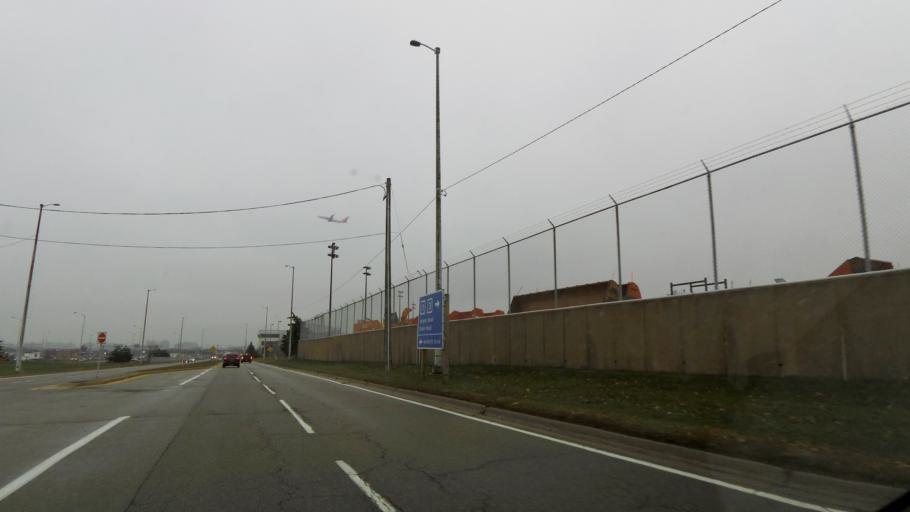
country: CA
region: Ontario
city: Etobicoke
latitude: 43.6838
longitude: -79.6004
